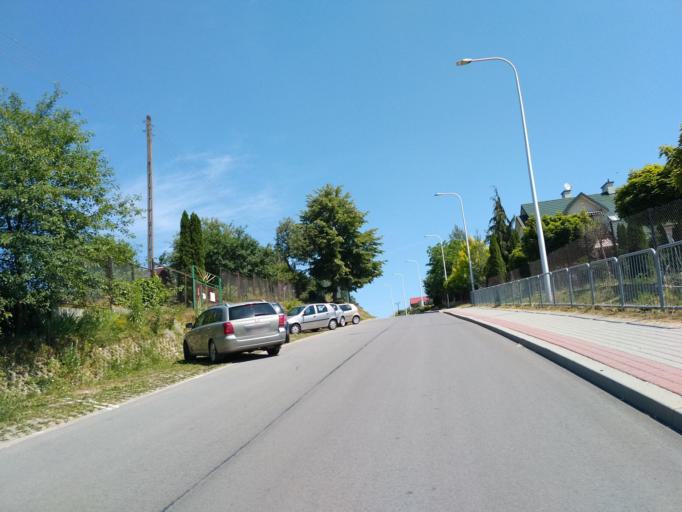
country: PL
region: Subcarpathian Voivodeship
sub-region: Krosno
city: Krosno
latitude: 49.7055
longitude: 21.7697
